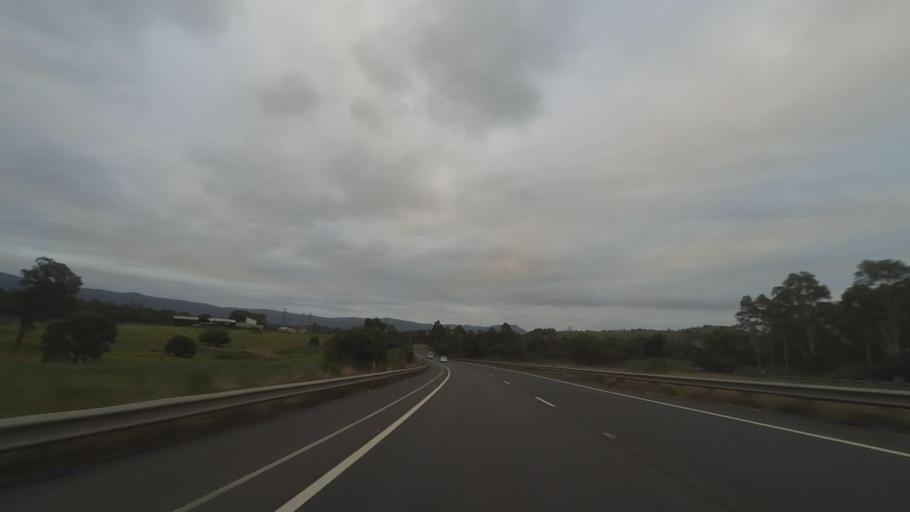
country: AU
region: New South Wales
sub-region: Shellharbour
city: Albion Park Rail
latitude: -34.5349
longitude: 150.7861
